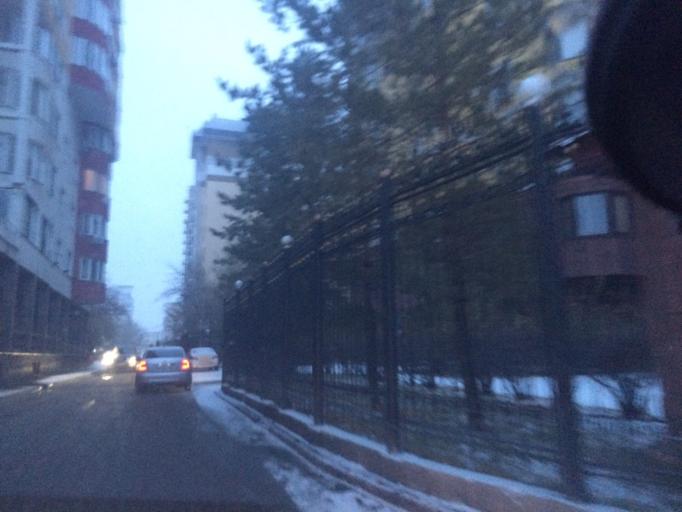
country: KZ
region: Astana Qalasy
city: Astana
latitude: 51.1604
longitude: 71.4246
